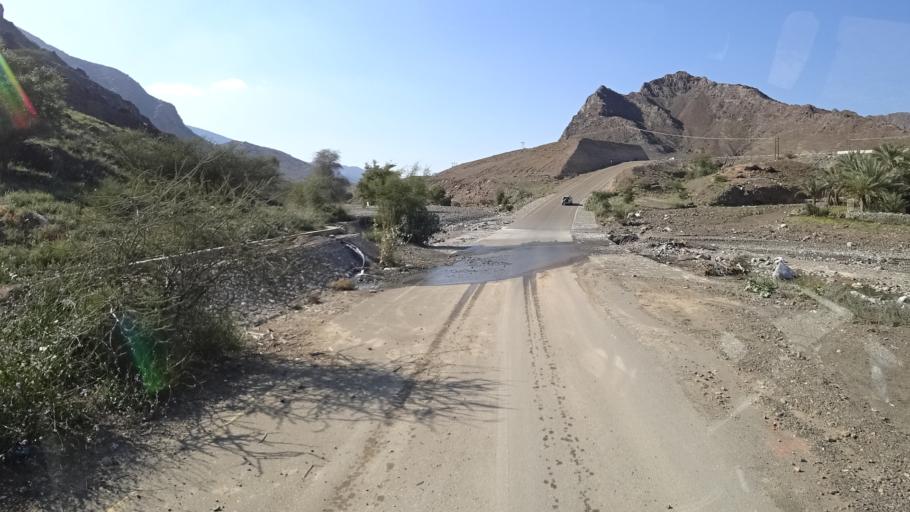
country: OM
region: Al Batinah
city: Rustaq
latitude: 23.4578
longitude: 57.0837
